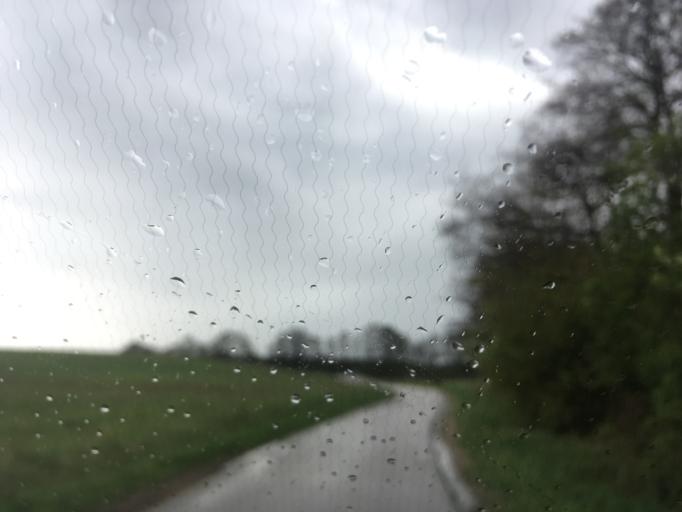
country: PL
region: Warmian-Masurian Voivodeship
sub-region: Powiat dzialdowski
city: Rybno
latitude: 53.3802
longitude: 19.9906
